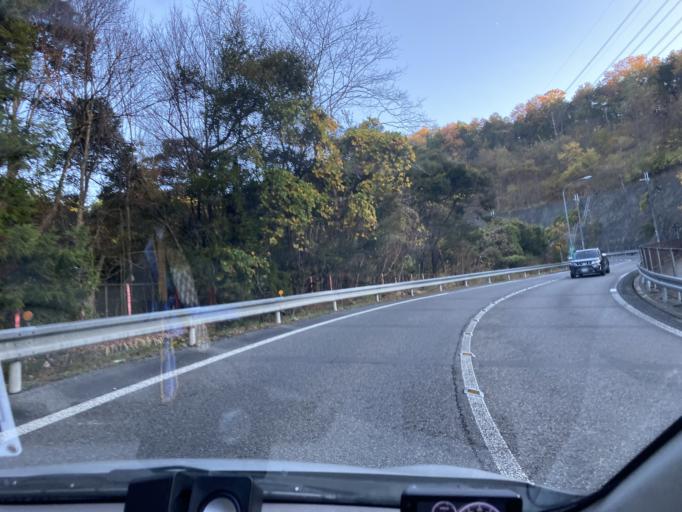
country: JP
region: Kyoto
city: Uji
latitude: 34.9188
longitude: 135.8809
